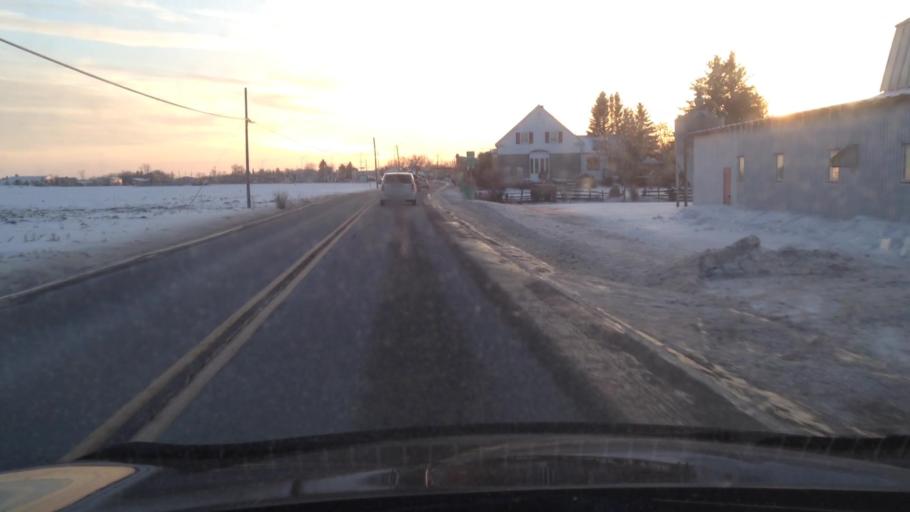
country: CA
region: Quebec
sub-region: Lanaudiere
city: Saint-Lin-Laurentides
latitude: 45.8990
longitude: -73.7526
